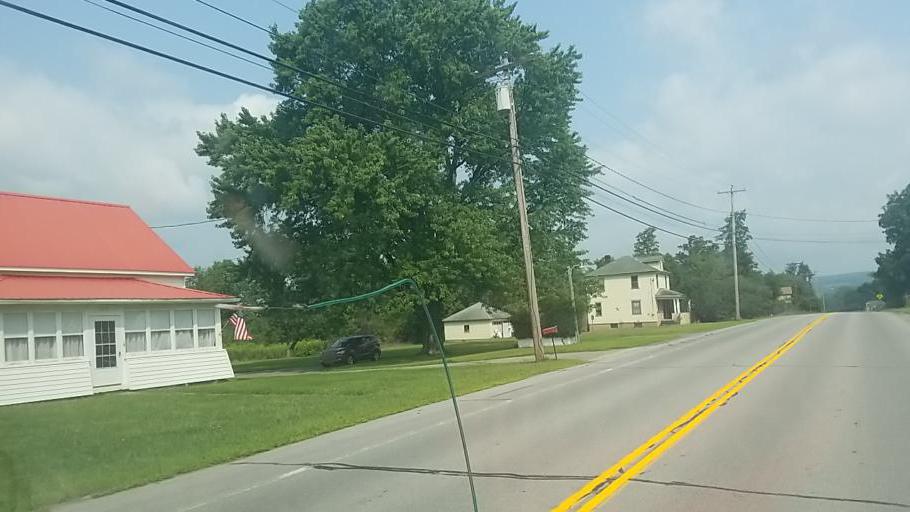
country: US
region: New York
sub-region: Montgomery County
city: Fort Plain
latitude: 42.9517
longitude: -74.6204
